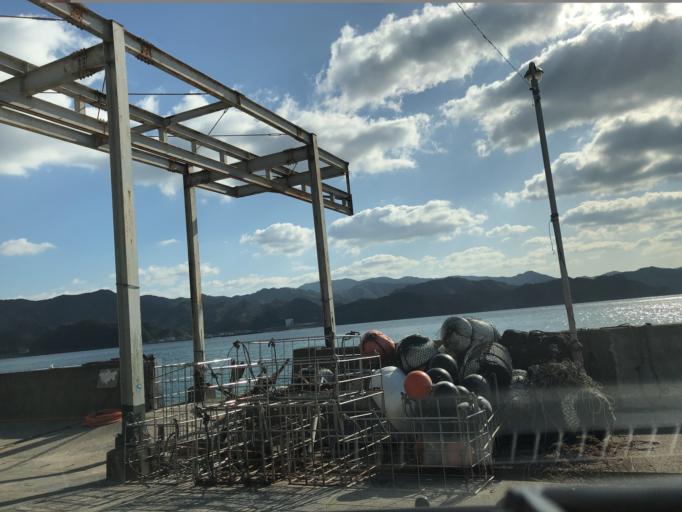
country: JP
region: Kochi
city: Sukumo
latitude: 32.9121
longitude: 132.7014
